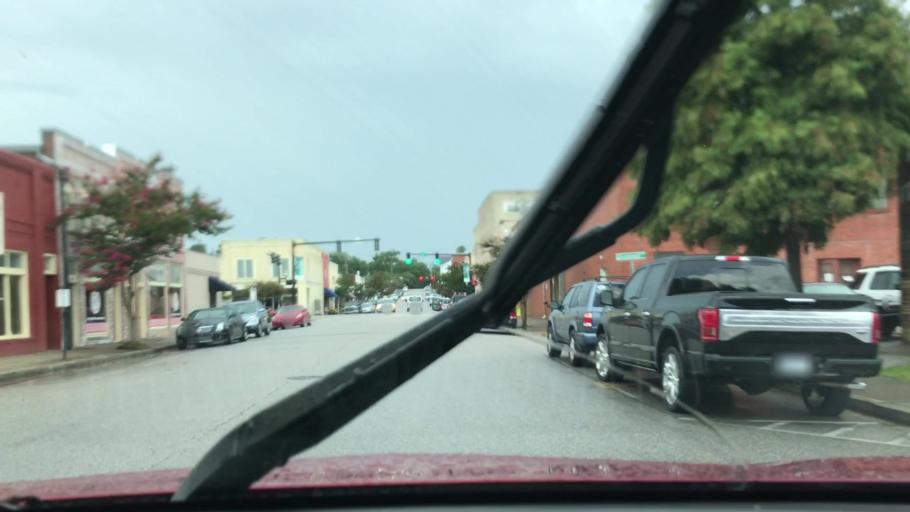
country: US
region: South Carolina
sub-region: Horry County
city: Conway
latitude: 33.8341
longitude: -79.0467
